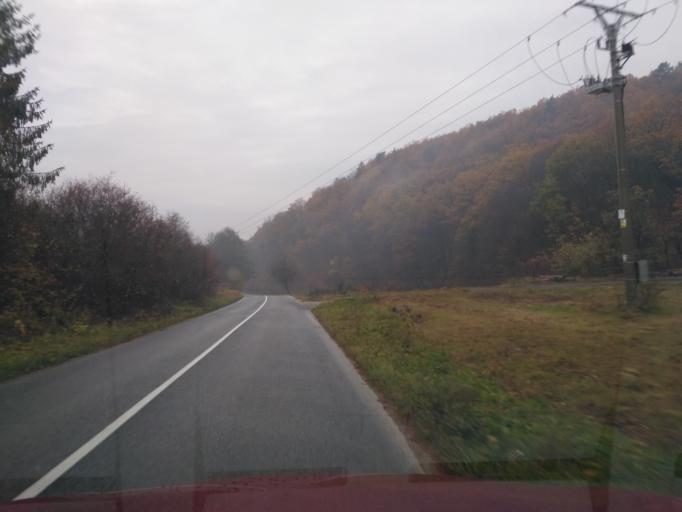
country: SK
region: Kosicky
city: Medzev
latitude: 48.7094
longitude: 20.8690
